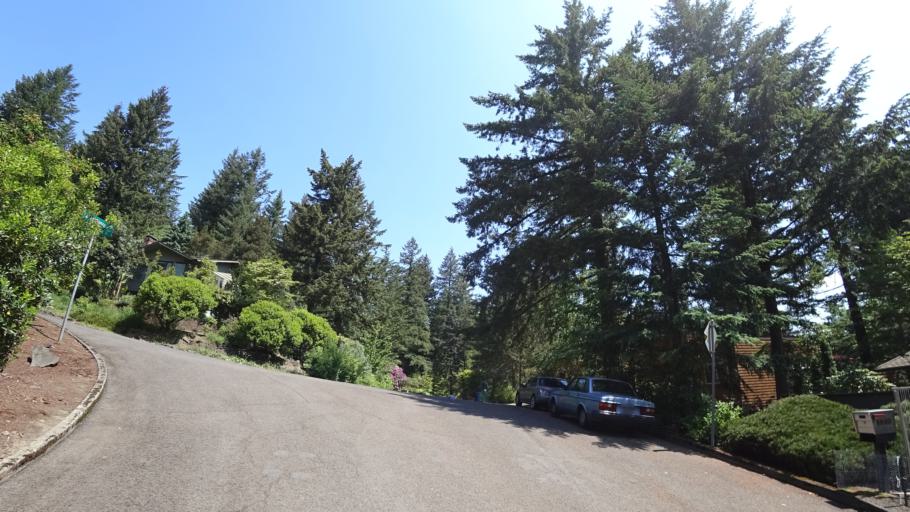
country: US
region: Oregon
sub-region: Washington County
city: West Slope
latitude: 45.5136
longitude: -122.7275
